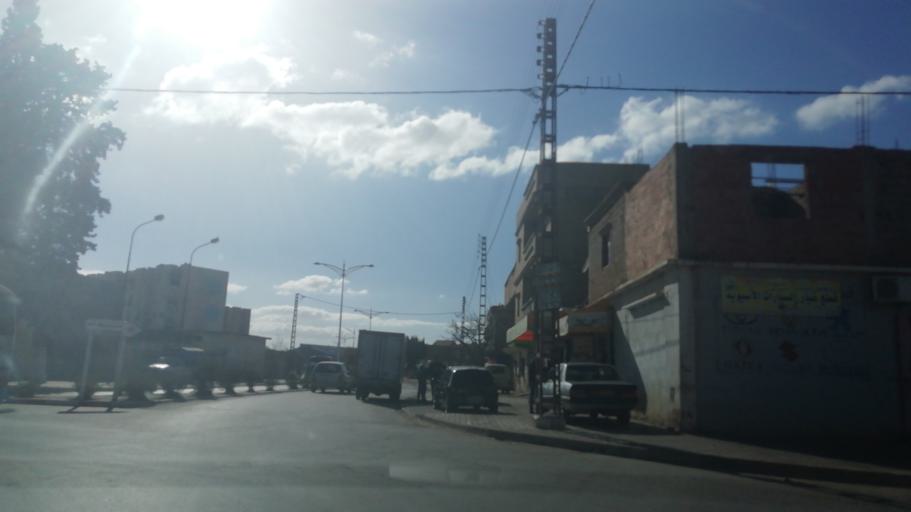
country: DZ
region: Mostaganem
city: Mostaganem
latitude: 35.9940
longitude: 0.2963
